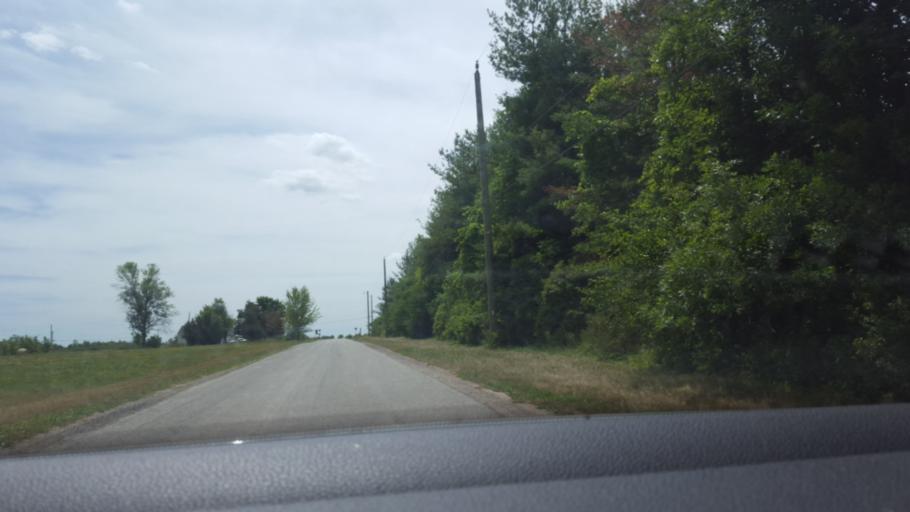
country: CA
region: Ontario
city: Hamilton
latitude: 43.1875
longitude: -79.5761
